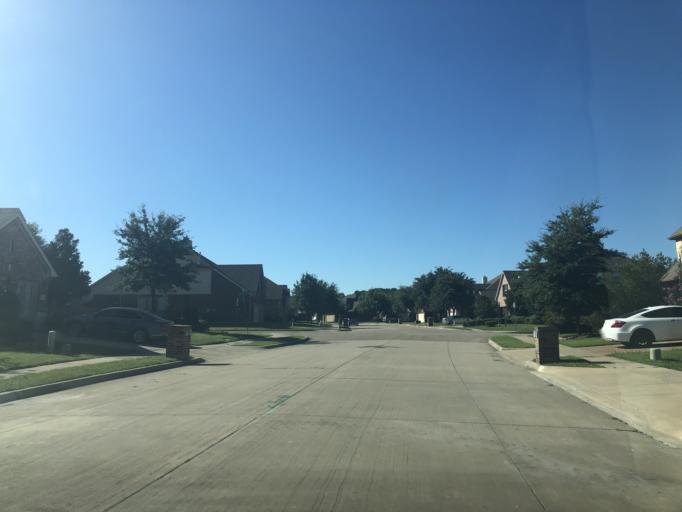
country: US
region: Texas
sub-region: Dallas County
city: Duncanville
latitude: 32.6601
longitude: -96.9701
